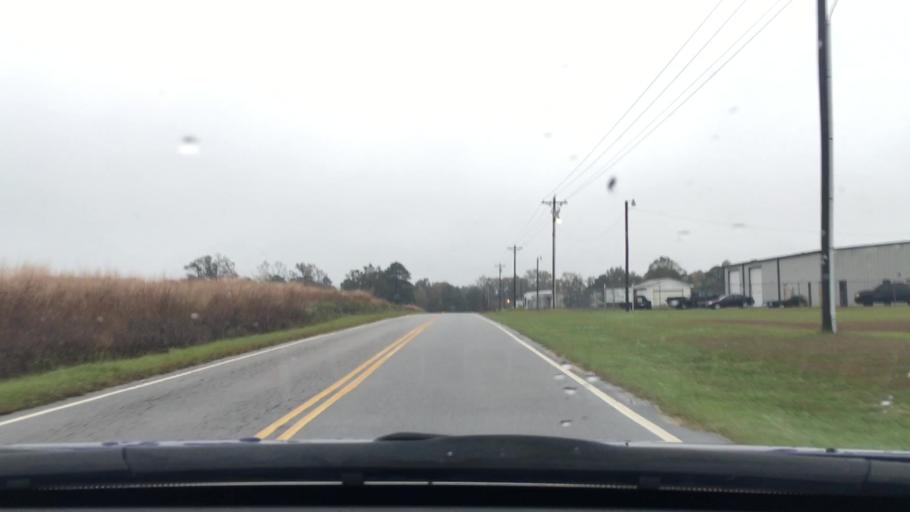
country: US
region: South Carolina
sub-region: Darlington County
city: Darlington
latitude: 34.2981
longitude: -79.9226
